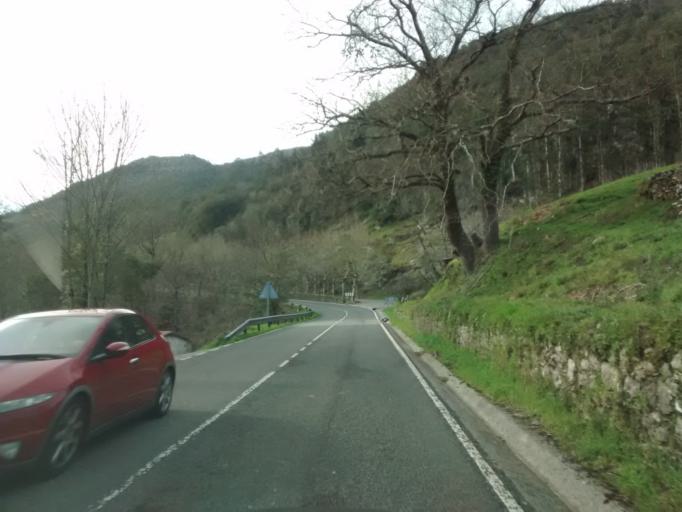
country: ES
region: Cantabria
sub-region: Provincia de Cantabria
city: Arredondo
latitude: 43.2770
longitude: -3.6059
